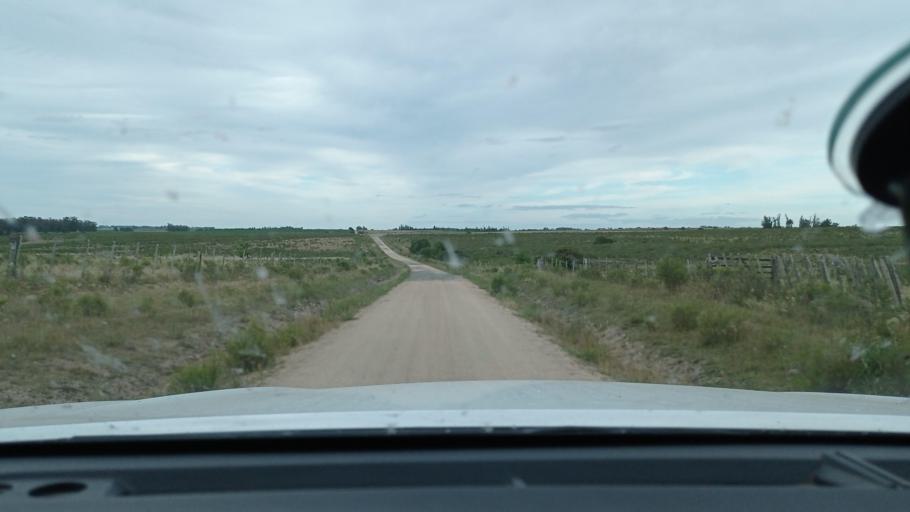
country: UY
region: Florida
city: Casupa
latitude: -34.1439
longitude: -55.7892
